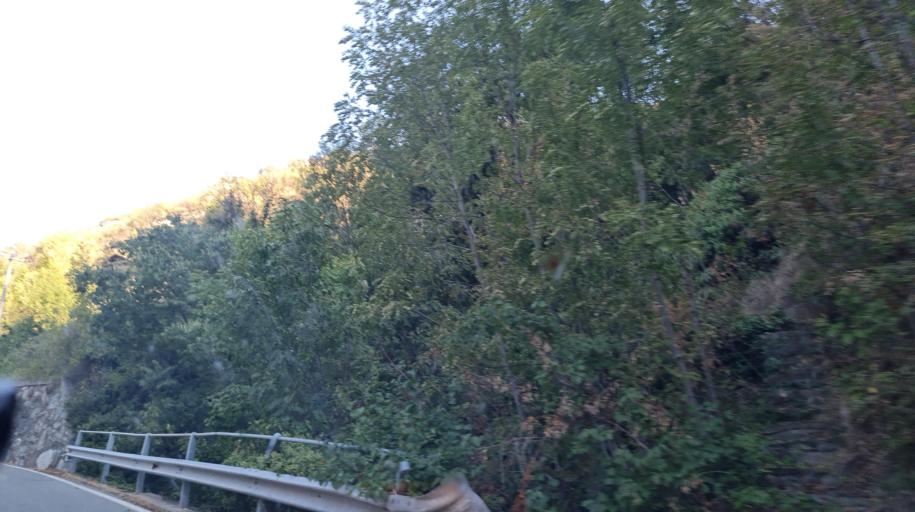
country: IT
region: Aosta Valley
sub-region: Valle d'Aosta
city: Arnad
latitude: 45.6397
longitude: 7.7381
